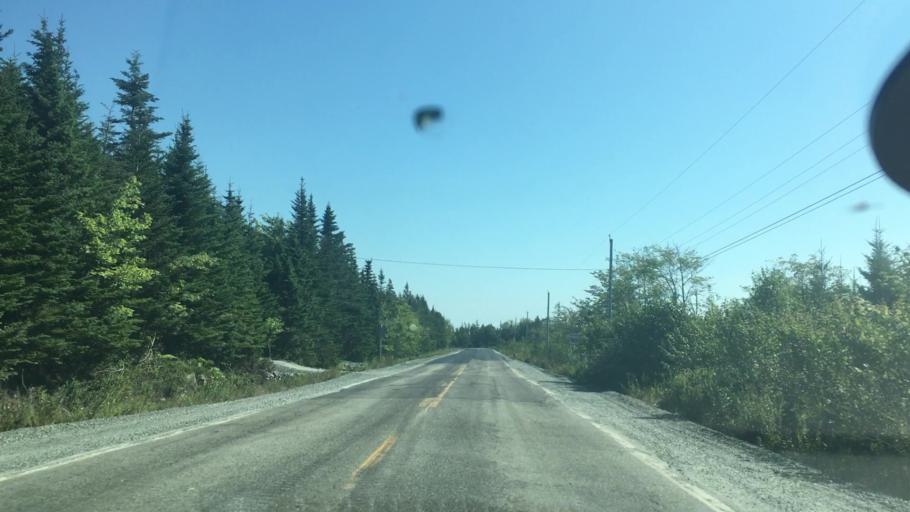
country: CA
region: Nova Scotia
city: New Glasgow
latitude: 44.8982
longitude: -62.4252
